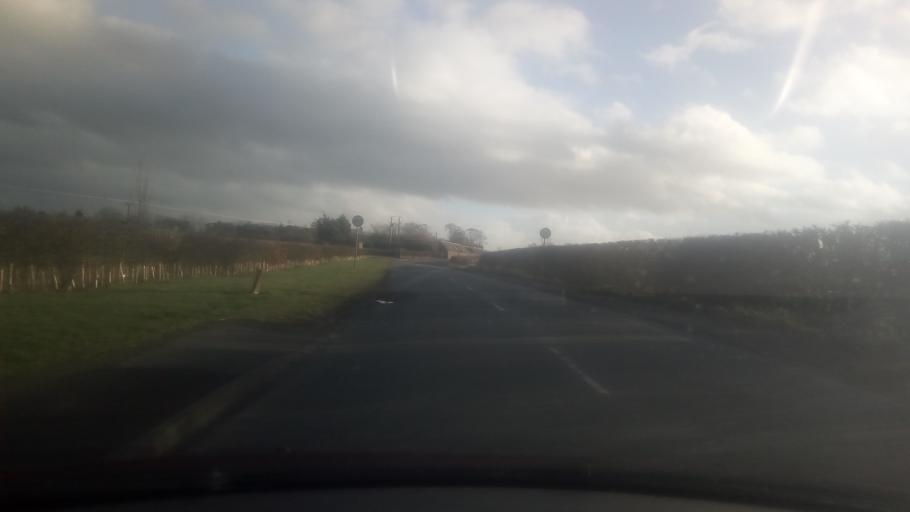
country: GB
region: Scotland
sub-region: The Scottish Borders
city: Kelso
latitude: 55.6144
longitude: -2.4260
